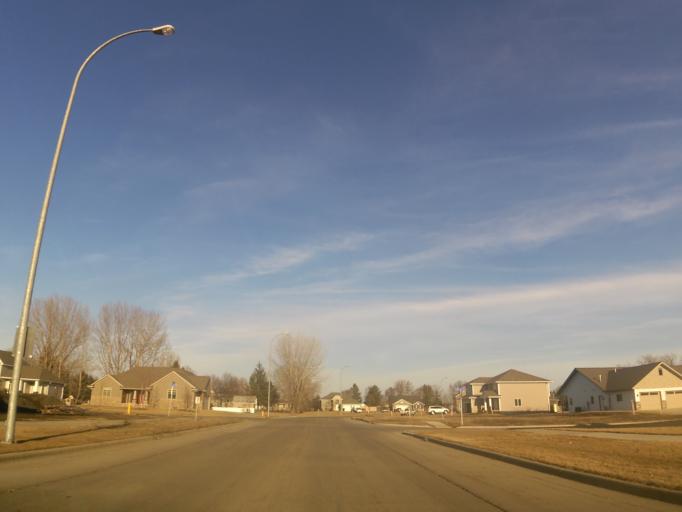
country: US
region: North Dakota
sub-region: Grand Forks County
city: Grand Forks
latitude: 47.8676
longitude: -97.0336
